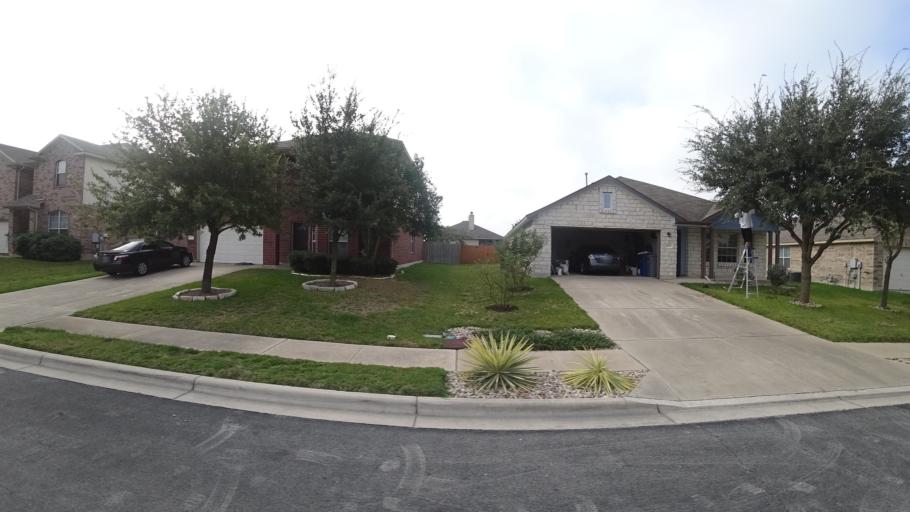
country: US
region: Texas
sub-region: Travis County
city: Pflugerville
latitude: 30.3586
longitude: -97.6441
